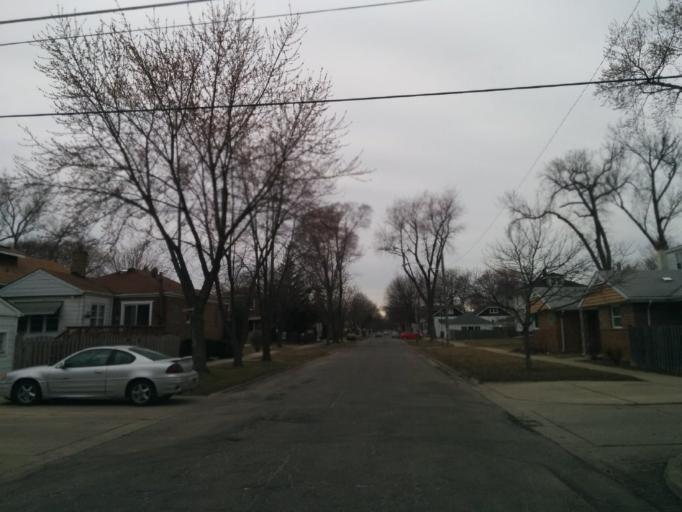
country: US
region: Illinois
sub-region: Cook County
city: Brookfield
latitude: 41.8313
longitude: -87.8484
